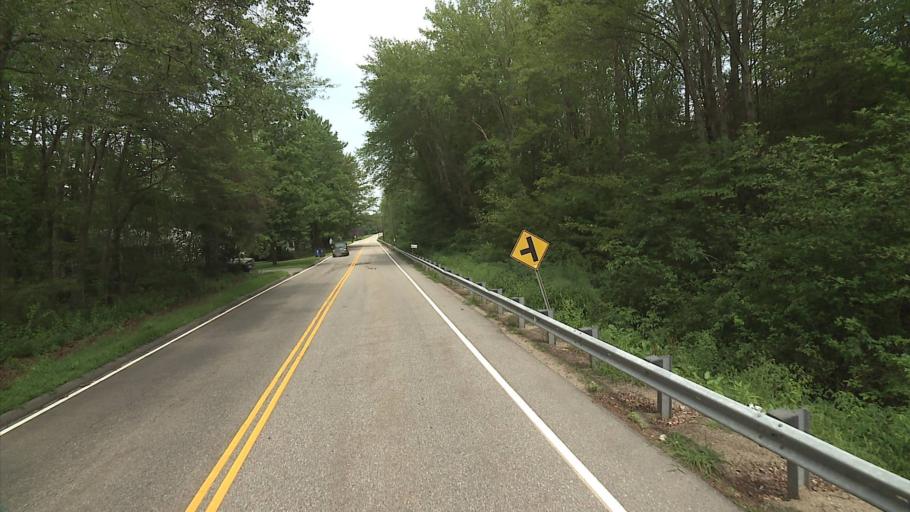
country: US
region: Connecticut
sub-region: Windham County
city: Danielson
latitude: 41.8045
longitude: -71.8733
